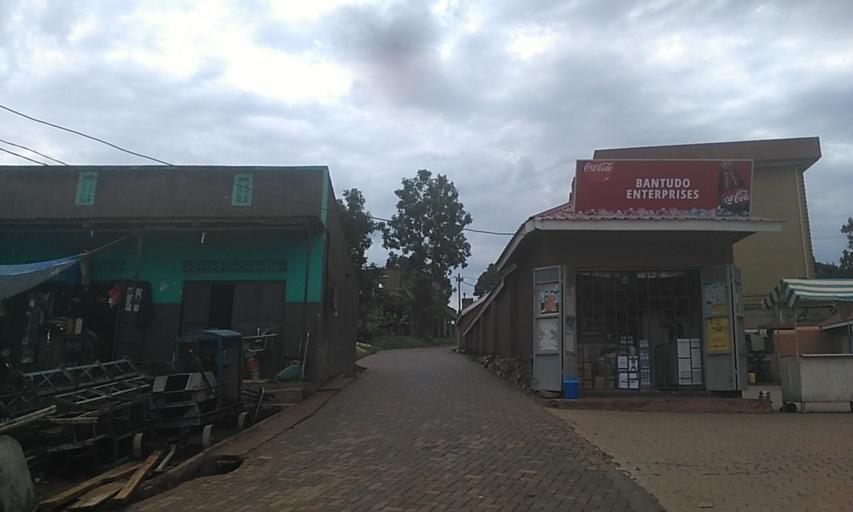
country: UG
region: Central Region
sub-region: Wakiso District
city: Bweyogerere
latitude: 0.3960
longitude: 32.6681
